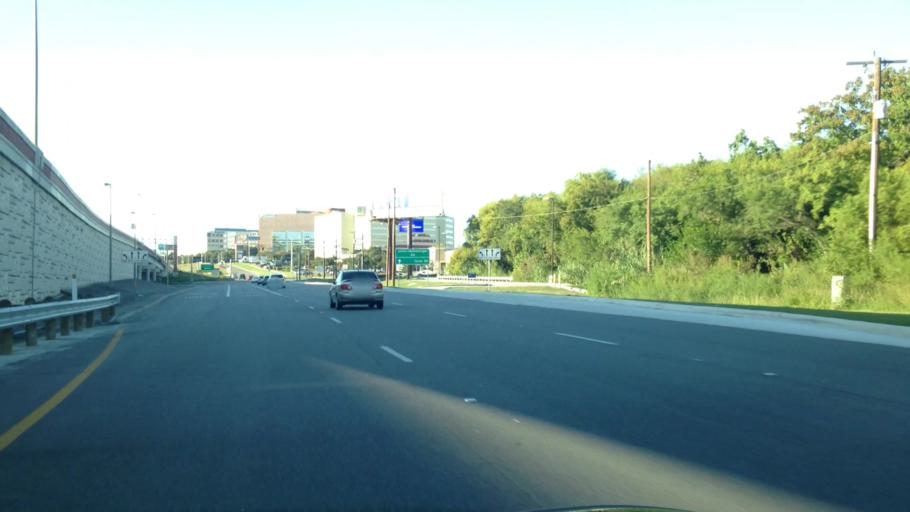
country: US
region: Texas
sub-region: Bexar County
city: Castle Hills
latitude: 29.5264
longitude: -98.4824
